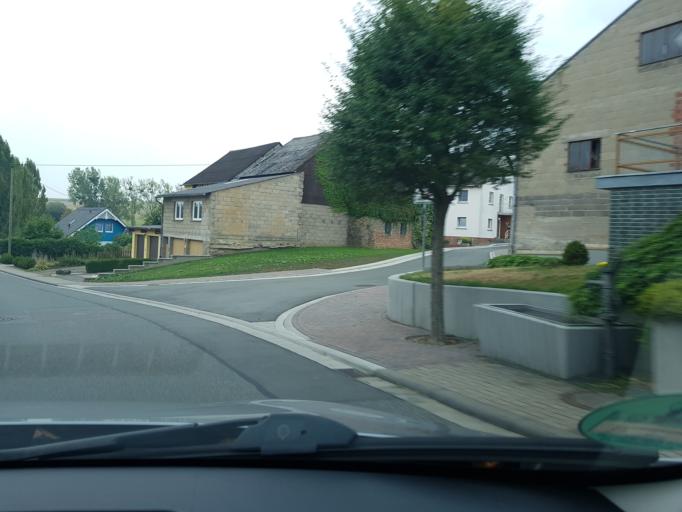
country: DE
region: Rheinland-Pfalz
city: Gemmerich
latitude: 50.2273
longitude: 7.7575
